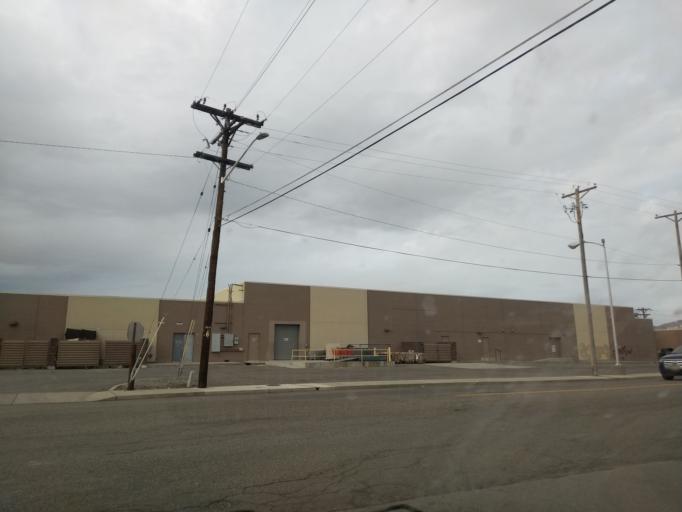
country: US
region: Colorado
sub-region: Mesa County
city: Grand Junction
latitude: 39.0754
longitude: -108.5374
